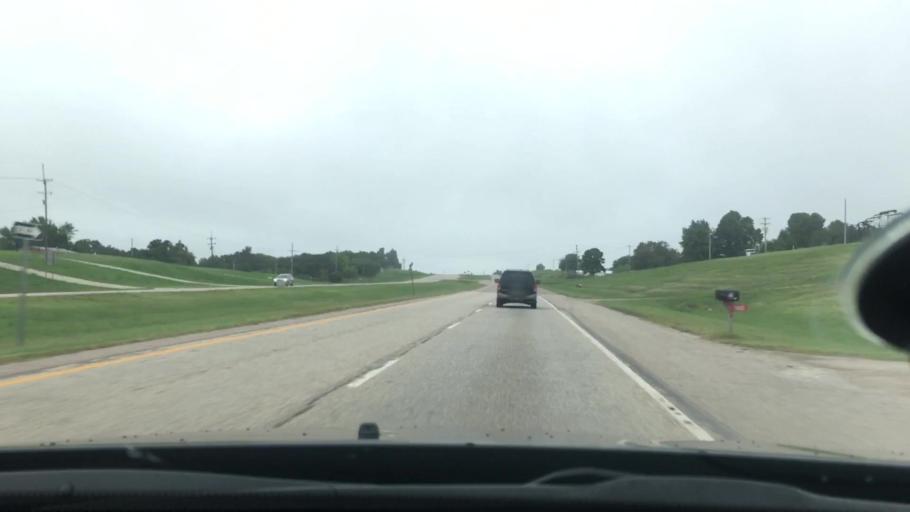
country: US
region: Oklahoma
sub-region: Seminole County
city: Seminole
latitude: 35.3013
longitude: -96.6707
